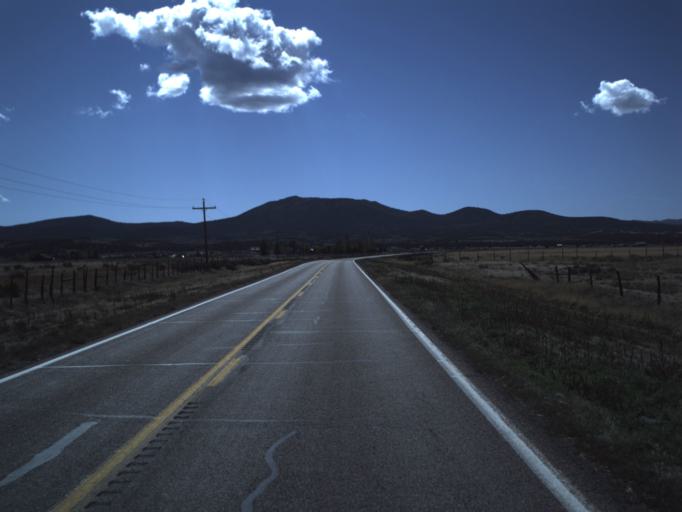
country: US
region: Utah
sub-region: Washington County
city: Enterprise
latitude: 37.6044
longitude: -113.6612
